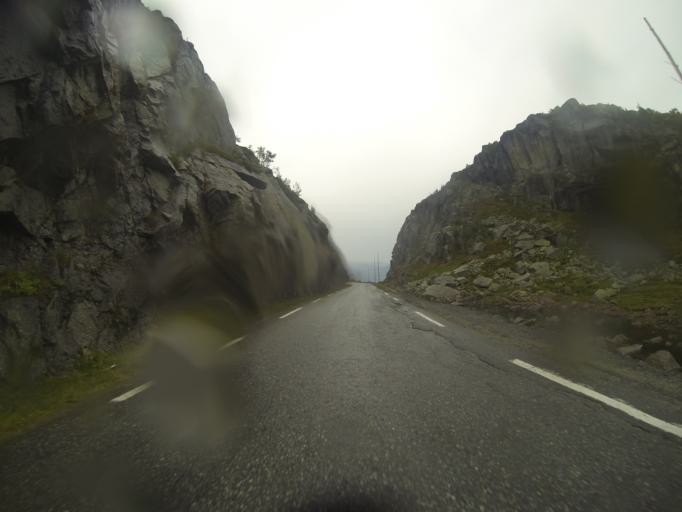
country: NO
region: Hordaland
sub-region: Odda
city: Odda
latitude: 59.7776
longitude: 6.7509
